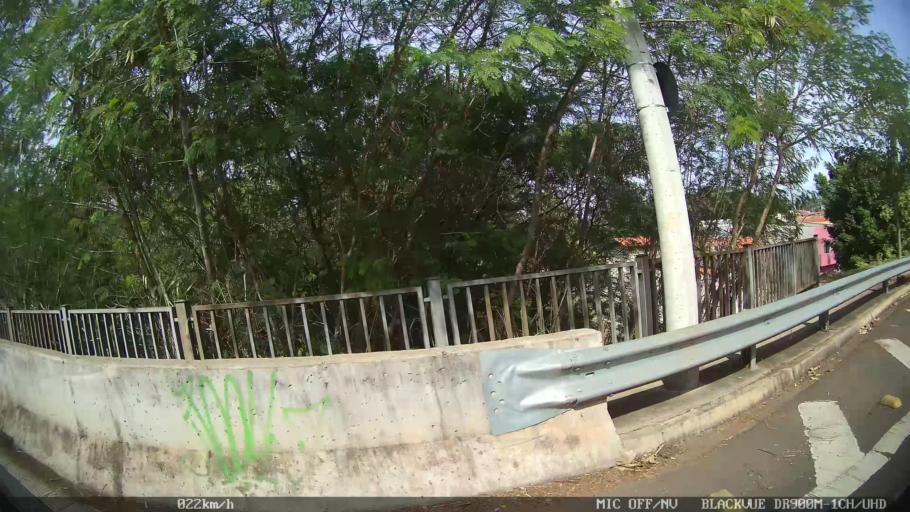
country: BR
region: Sao Paulo
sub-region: Piracicaba
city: Piracicaba
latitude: -22.7466
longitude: -47.6272
